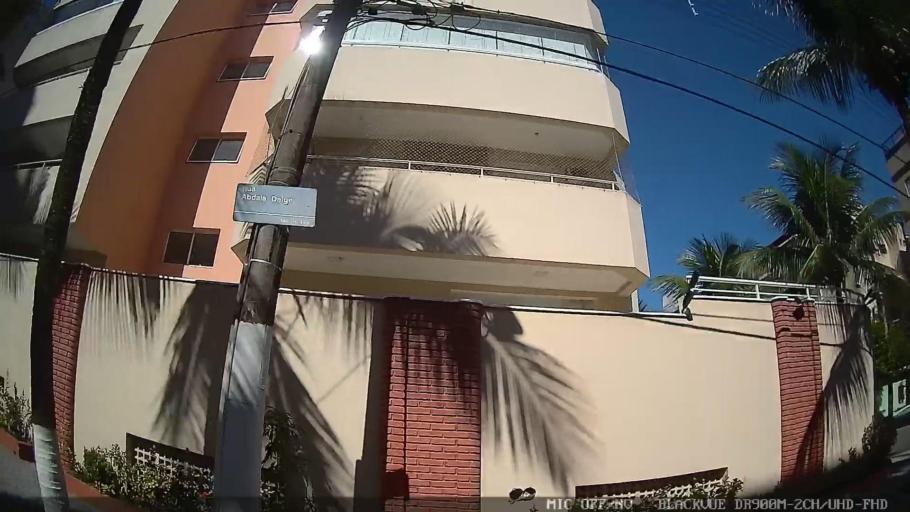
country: BR
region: Sao Paulo
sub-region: Guaruja
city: Guaruja
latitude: -23.9806
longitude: -46.2235
